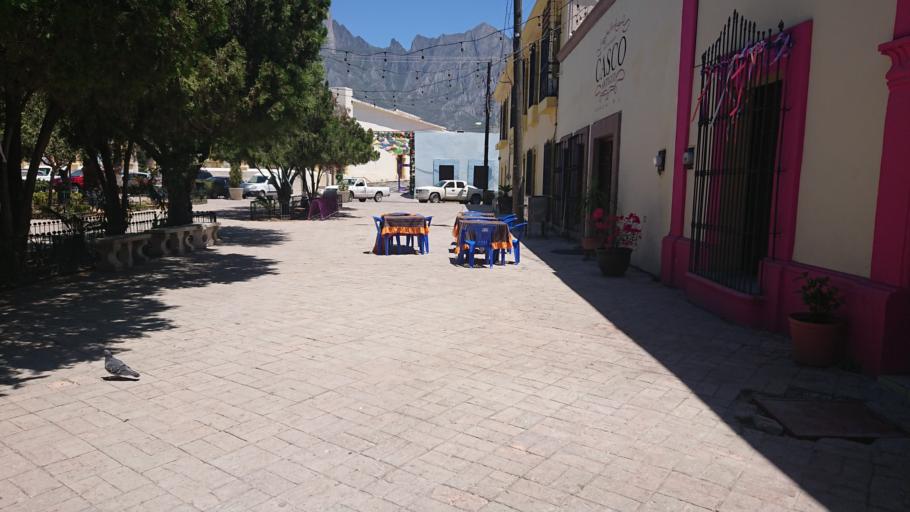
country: MX
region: Nuevo Leon
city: Garcia
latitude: 25.8114
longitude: -100.5944
